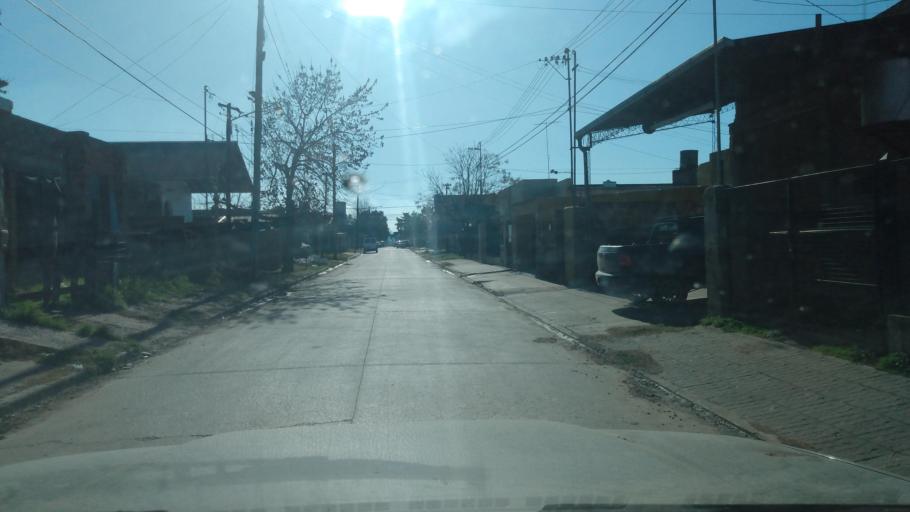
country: AR
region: Buenos Aires
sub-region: Partido de Lujan
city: Lujan
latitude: -34.5646
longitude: -59.0919
